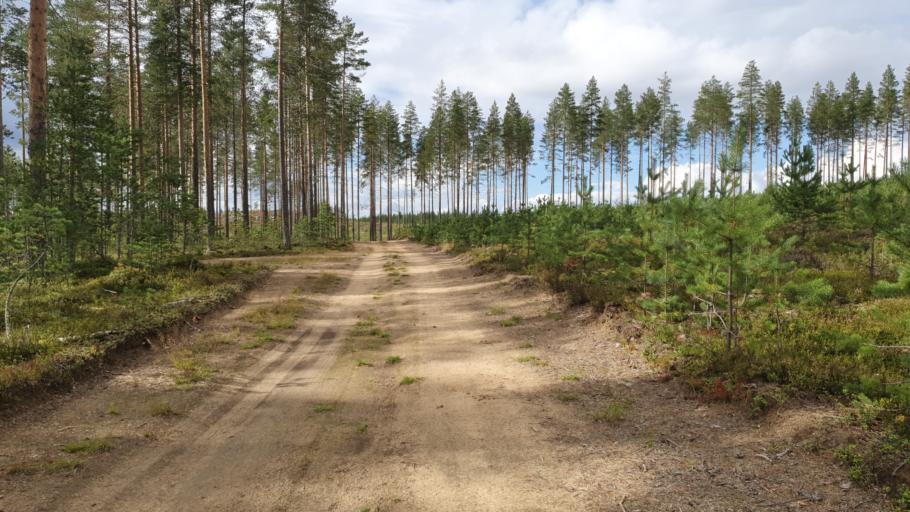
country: FI
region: Kainuu
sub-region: Kehys-Kainuu
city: Kuhmo
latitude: 64.1484
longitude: 29.3767
